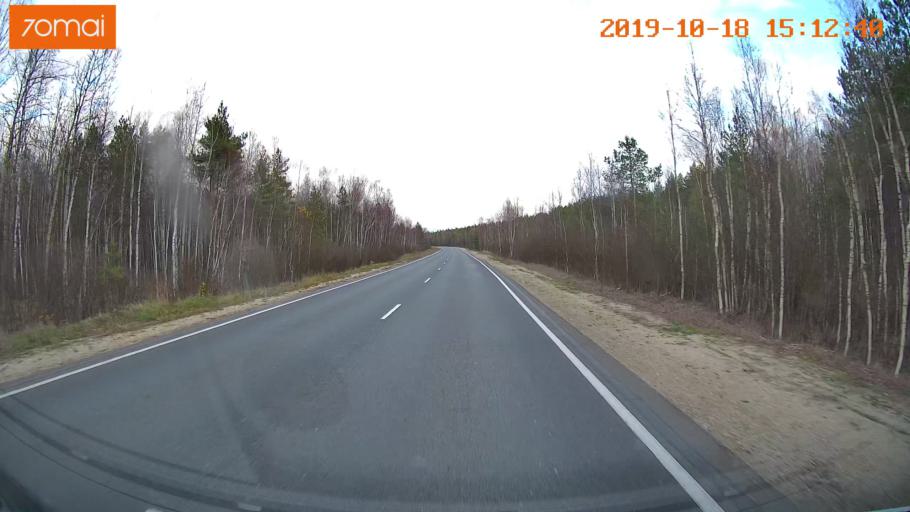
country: RU
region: Vladimir
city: Gus'-Khrustal'nyy
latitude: 55.5775
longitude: 40.7030
